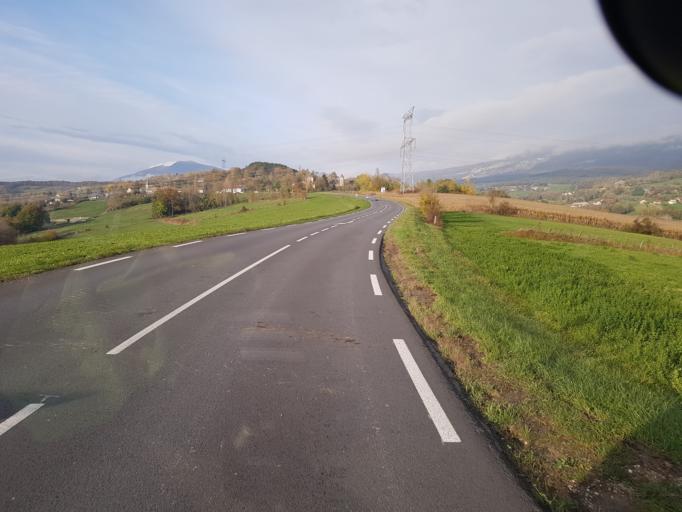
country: FR
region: Rhone-Alpes
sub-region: Departement de la Haute-Savoie
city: Frangy
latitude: 46.0358
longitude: 5.8880
